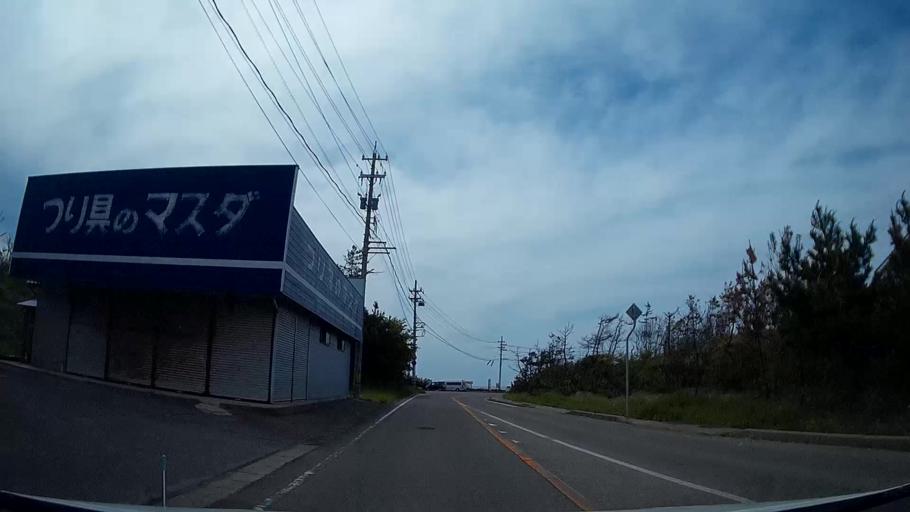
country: JP
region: Ishikawa
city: Hakui
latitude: 36.9973
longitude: 136.7722
